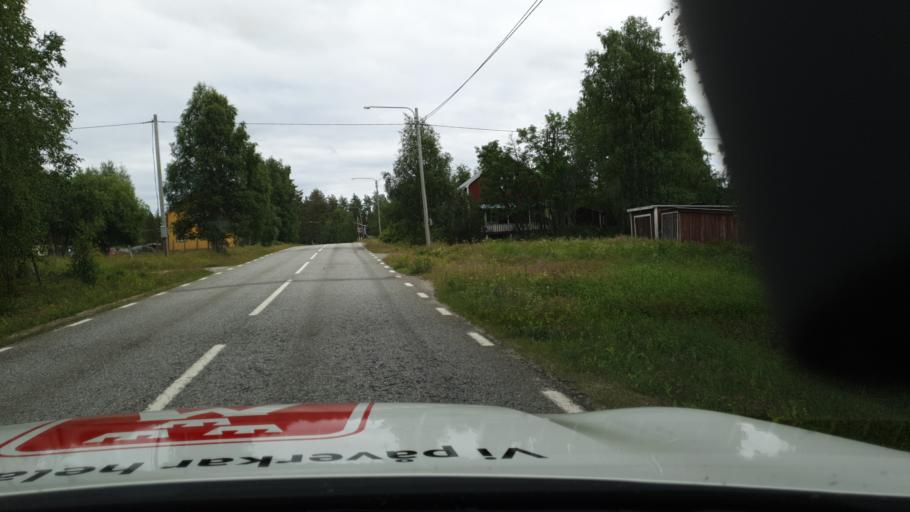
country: SE
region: Vaesterbotten
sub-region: Lycksele Kommun
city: Soderfors
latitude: 64.6267
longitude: 18.0679
